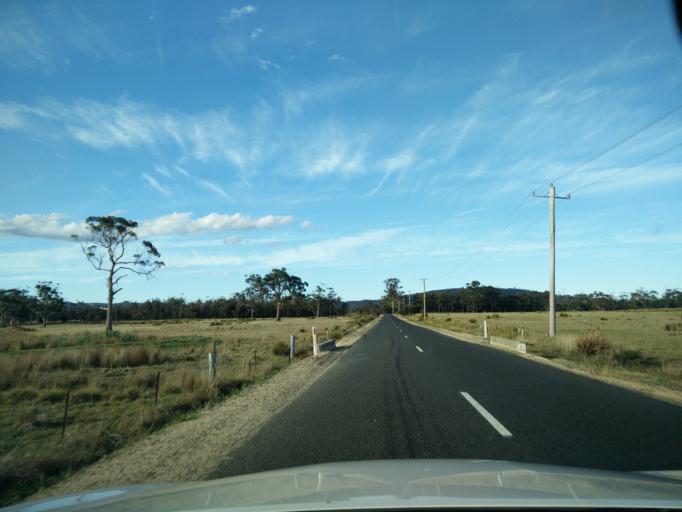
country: AU
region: Tasmania
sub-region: Break O'Day
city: St Helens
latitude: -41.9035
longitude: 148.2540
